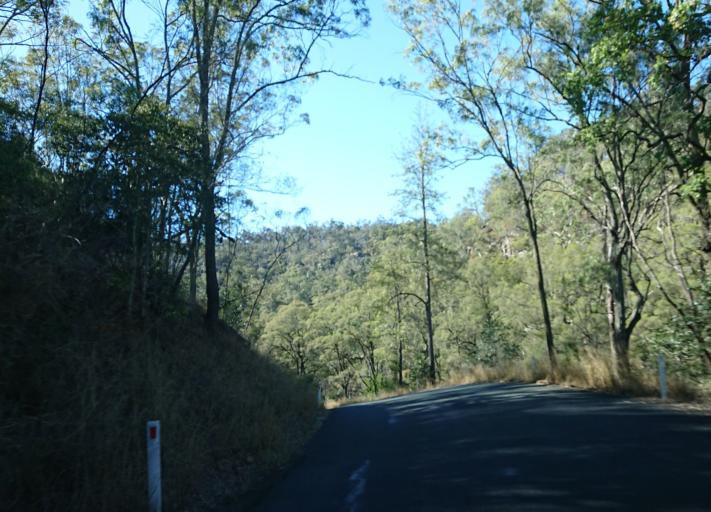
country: AU
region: Queensland
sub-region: Toowoomba
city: Top Camp
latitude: -27.7667
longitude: 152.0852
